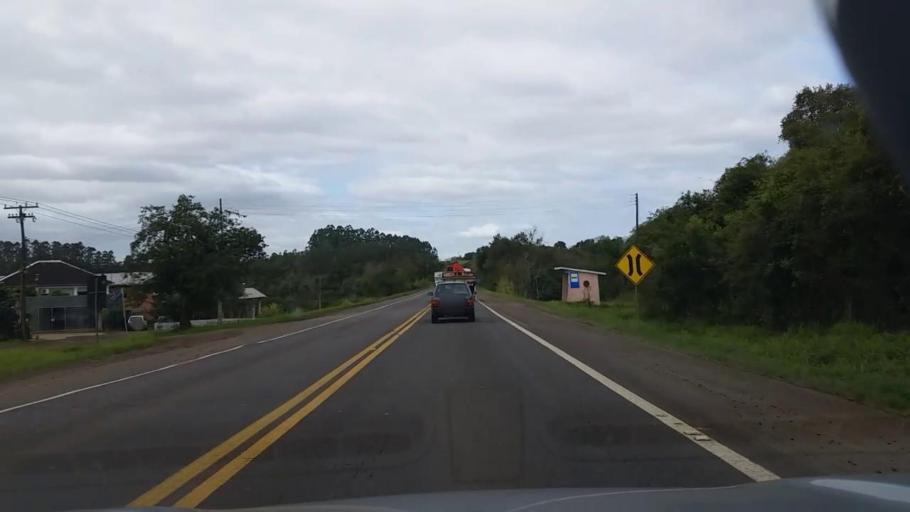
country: BR
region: Rio Grande do Sul
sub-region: Arroio Do Meio
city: Arroio do Meio
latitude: -29.4091
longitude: -52.0304
